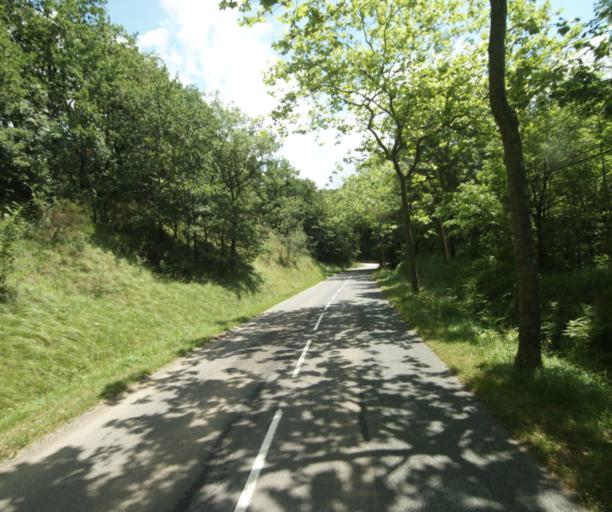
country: FR
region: Midi-Pyrenees
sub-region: Departement du Tarn
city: Soreze
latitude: 43.4352
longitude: 2.0466
